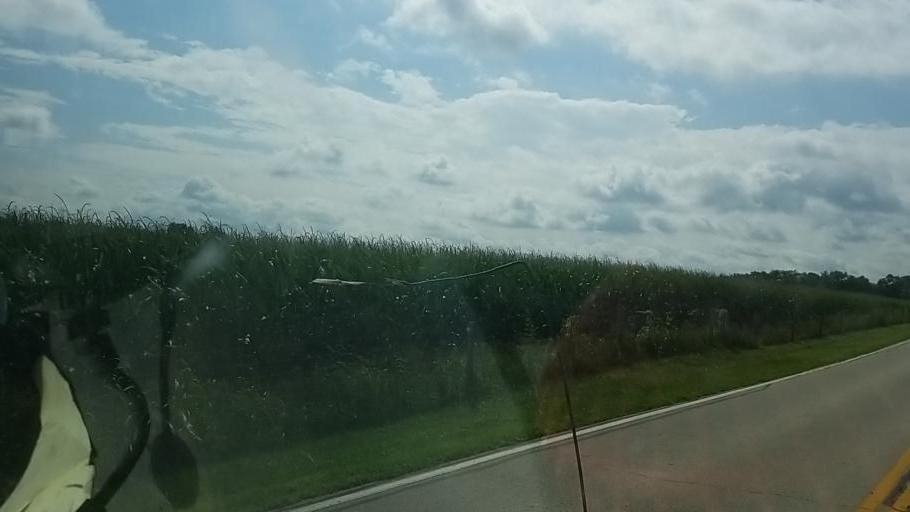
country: US
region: Ohio
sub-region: Pickaway County
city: Commercial Point
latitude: 39.7826
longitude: -83.1646
